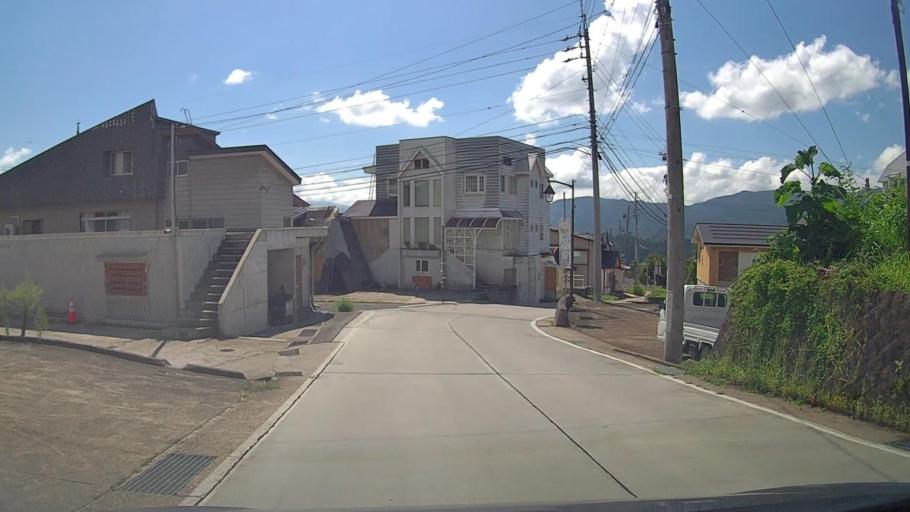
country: JP
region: Nagano
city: Iiyama
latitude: 36.9223
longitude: 138.4432
